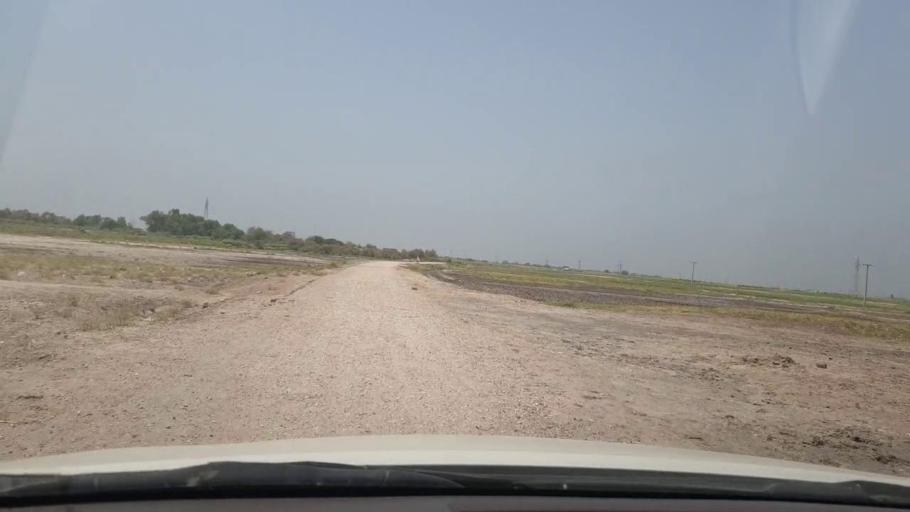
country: PK
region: Sindh
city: Shikarpur
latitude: 28.0263
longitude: 68.6176
